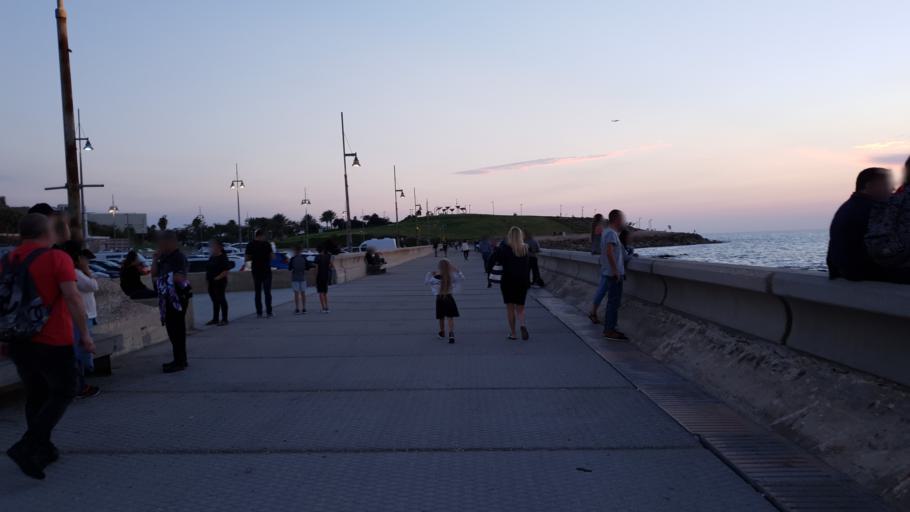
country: IL
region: Tel Aviv
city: Yafo
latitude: 32.0498
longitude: 34.7479
